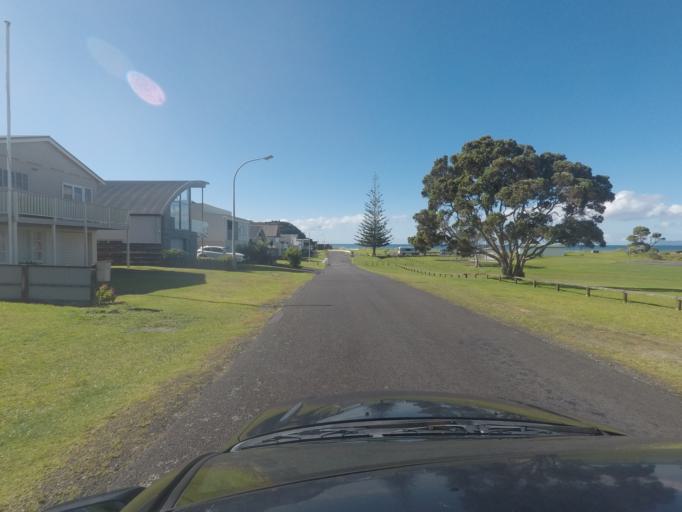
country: NZ
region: Bay of Plenty
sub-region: Western Bay of Plenty District
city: Waihi Beach
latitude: -37.4014
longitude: 175.9390
